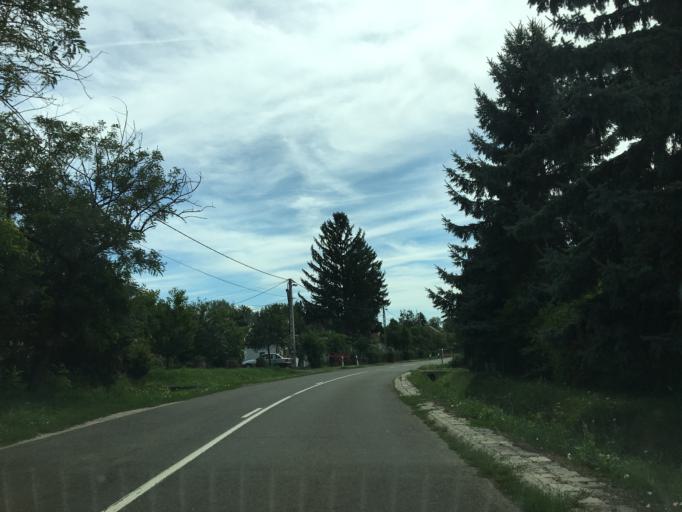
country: HU
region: Pest
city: Szob
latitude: 47.8436
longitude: 18.8267
